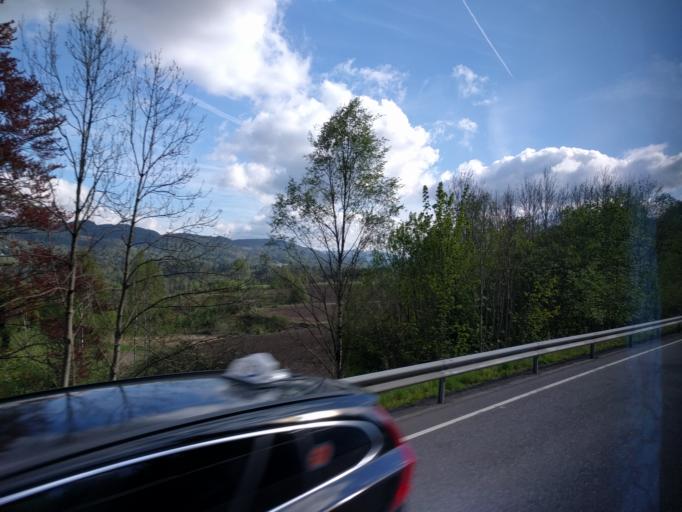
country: NO
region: Vestfold
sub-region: Lardal
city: Svarstad
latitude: 59.3670
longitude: 9.9229
